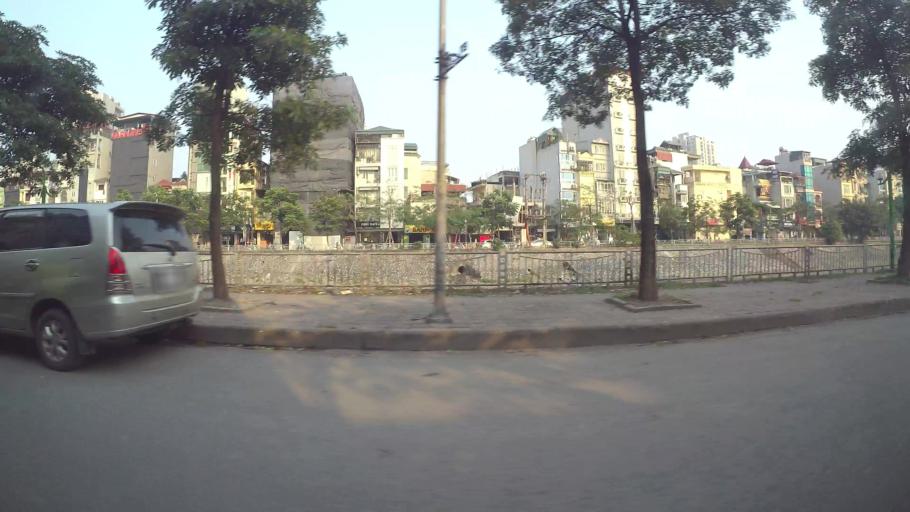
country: VN
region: Ha Noi
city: Thanh Xuan
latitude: 20.9981
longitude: 105.8166
